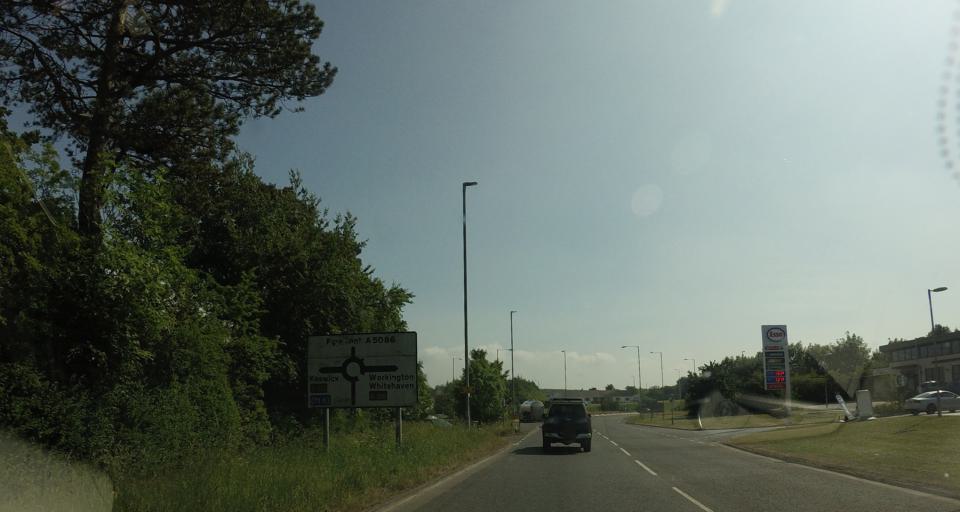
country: GB
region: England
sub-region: Cumbria
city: Cockermouth
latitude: 54.6540
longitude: -3.3722
